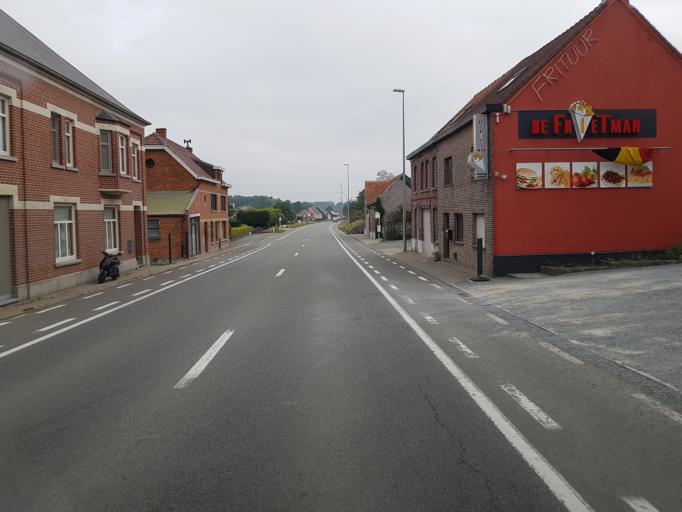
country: BE
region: Flanders
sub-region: Provincie Oost-Vlaanderen
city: Ninove
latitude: 50.8363
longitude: 3.9501
